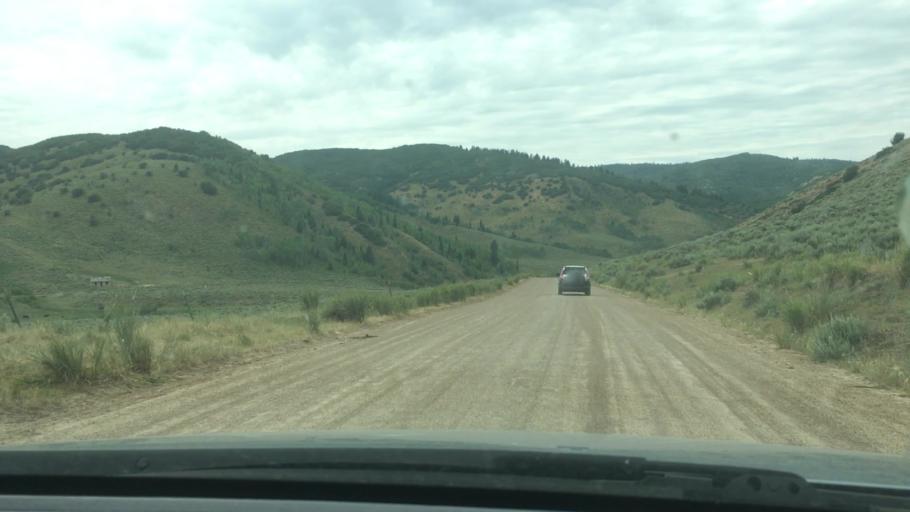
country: US
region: Utah
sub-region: Summit County
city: Summit Park
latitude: 40.7809
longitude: -111.5891
